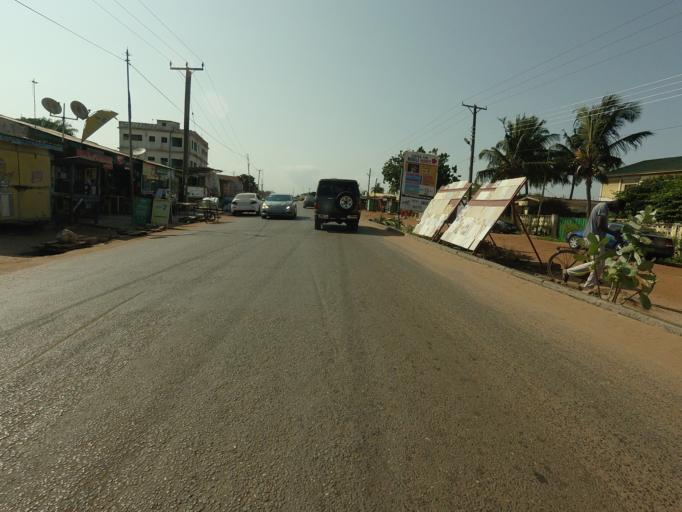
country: GH
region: Greater Accra
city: Teshi Old Town
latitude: 5.5980
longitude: -0.1024
